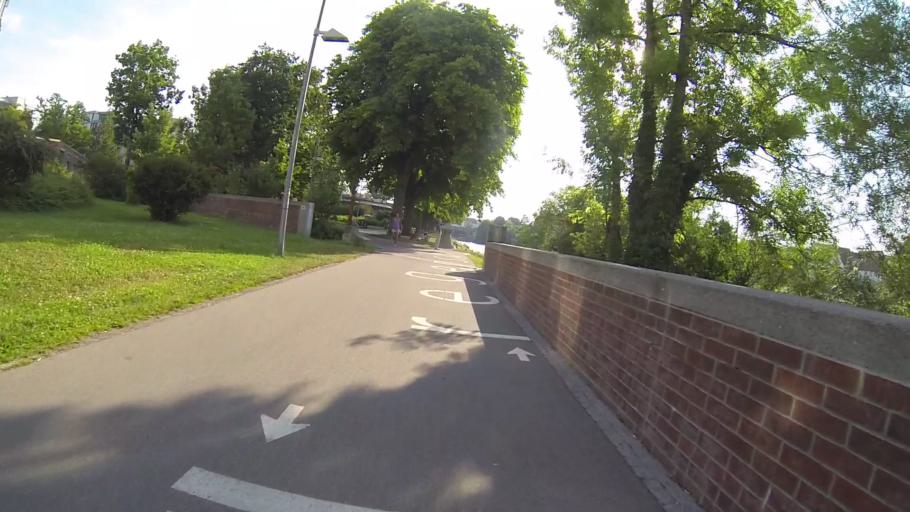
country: DE
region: Baden-Wuerttemberg
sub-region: Tuebingen Region
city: Ulm
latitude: 48.3945
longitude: 9.9932
